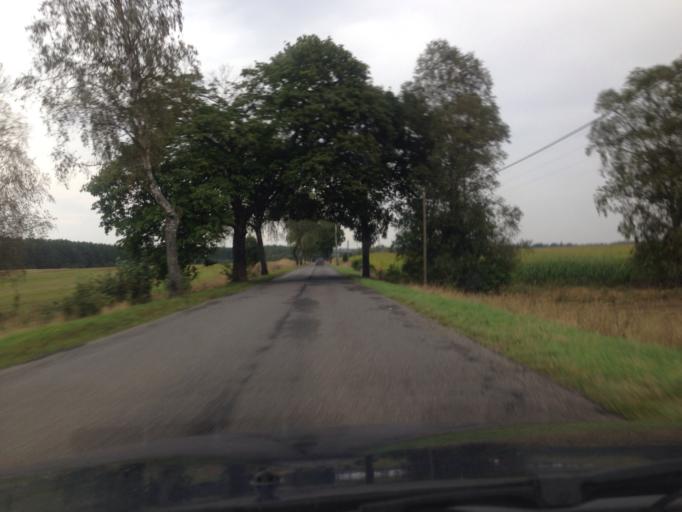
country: PL
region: Pomeranian Voivodeship
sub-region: Powiat bytowski
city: Czarna Dabrowka
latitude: 54.3608
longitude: 17.5332
